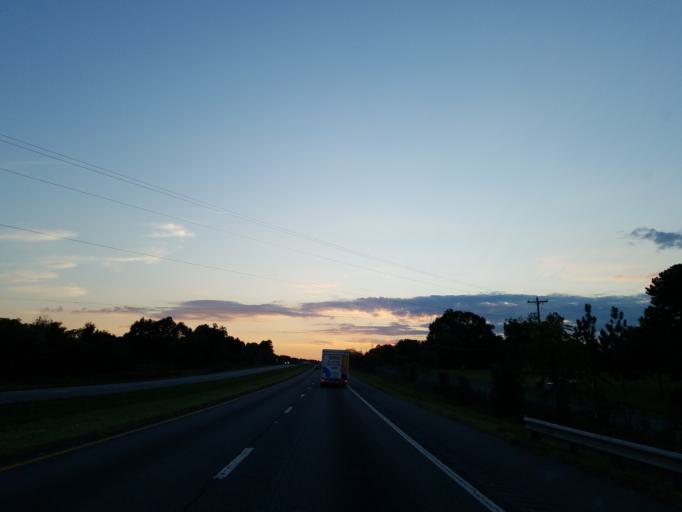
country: US
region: South Carolina
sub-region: Spartanburg County
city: Cowpens
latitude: 35.0740
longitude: -81.7497
